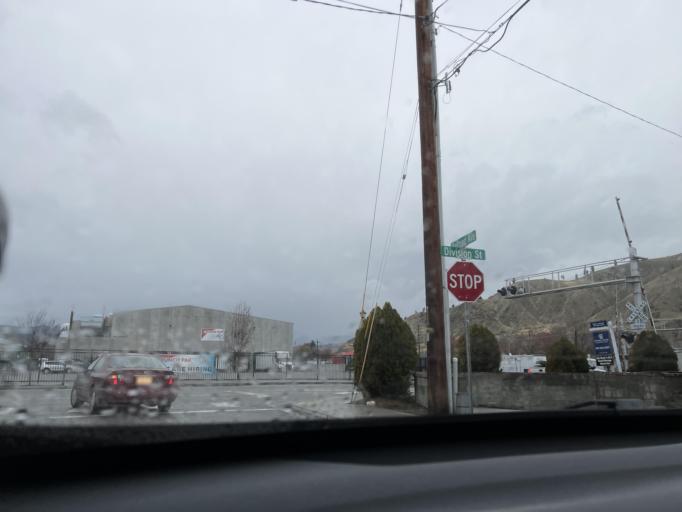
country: US
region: Washington
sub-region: Chelan County
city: Cashmere
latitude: 47.5205
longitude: -120.4696
